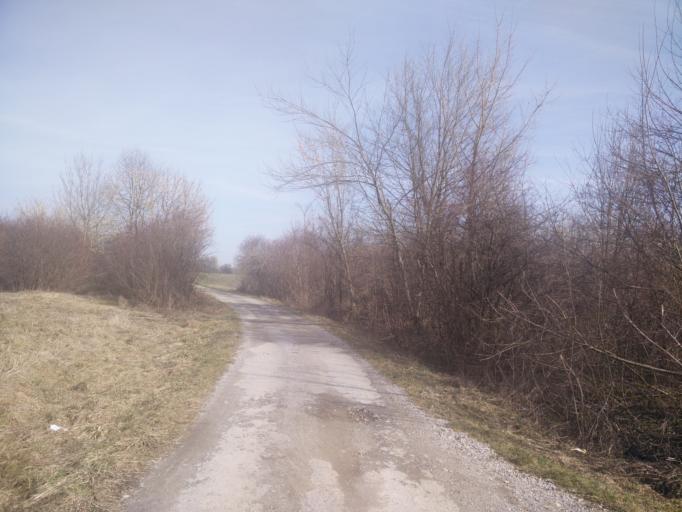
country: HR
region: Karlovacka
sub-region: Grad Karlovac
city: Karlovac
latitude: 45.5004
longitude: 15.5638
